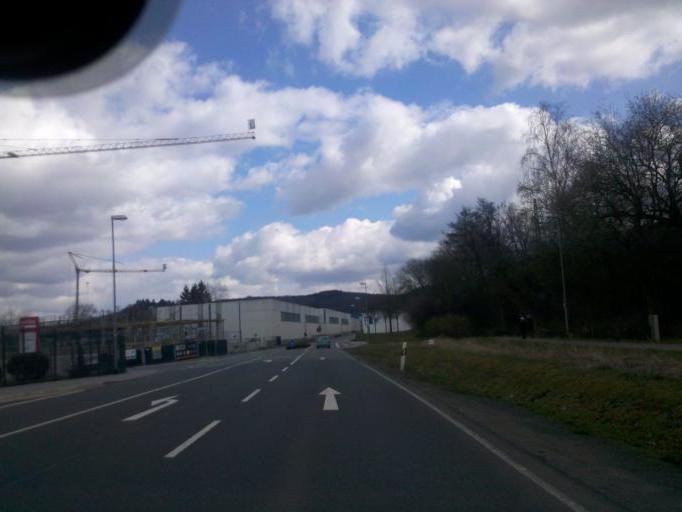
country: DE
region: Hesse
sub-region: Regierungsbezirk Giessen
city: Haiger
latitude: 50.7450
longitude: 8.2143
